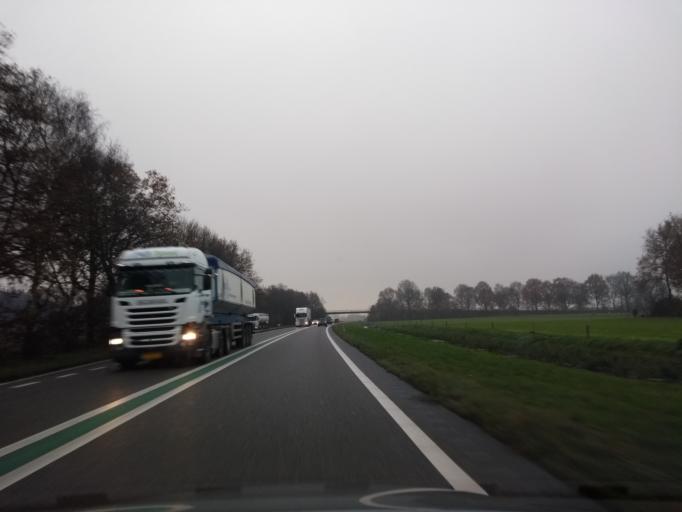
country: NL
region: Overijssel
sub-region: Gemeente Twenterand
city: Den Ham
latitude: 52.5683
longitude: 6.4214
